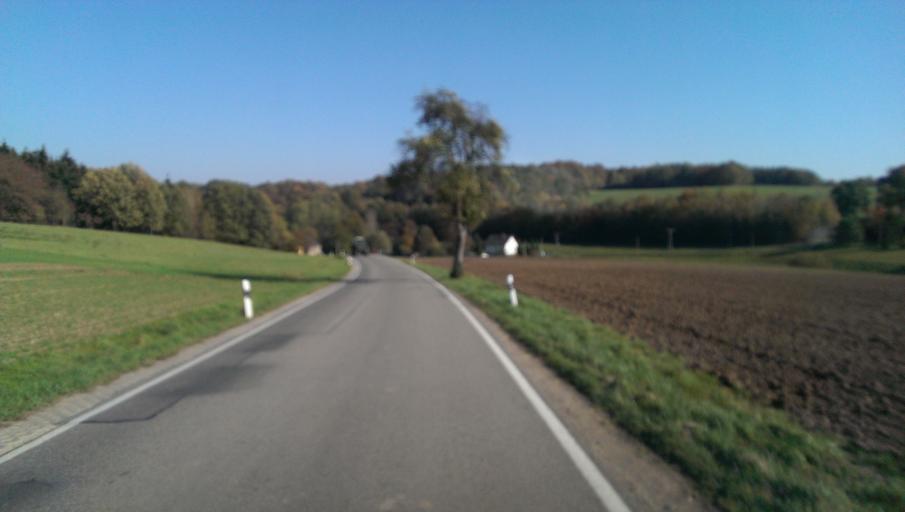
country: DE
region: Saxony
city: Kriebstein
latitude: 51.0611
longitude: 13.0051
